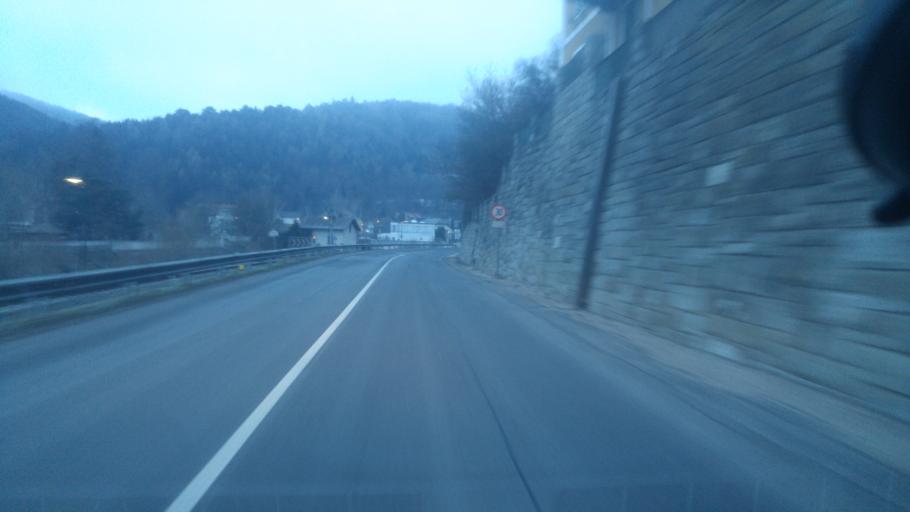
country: AT
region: Lower Austria
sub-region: Politischer Bezirk Baden
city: Weissenbach an der Triesting
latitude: 47.9839
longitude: 16.0388
